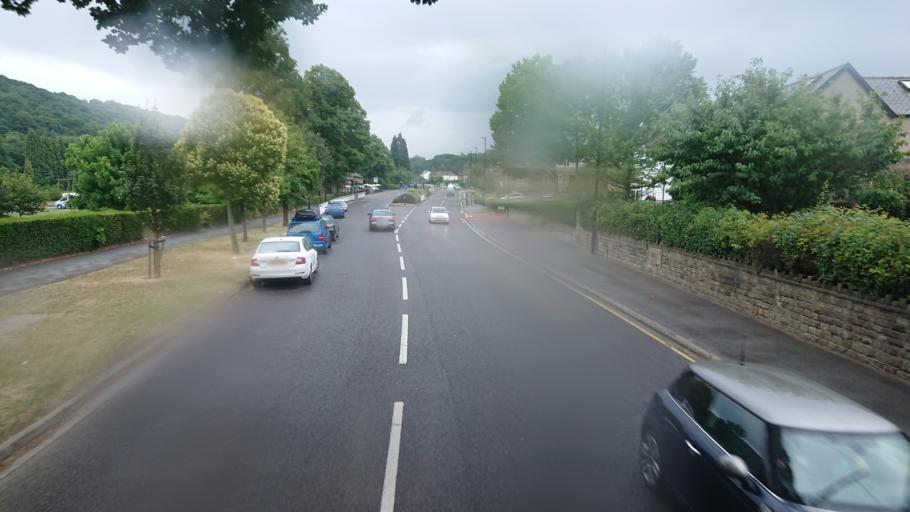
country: GB
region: England
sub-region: Derbyshire
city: Dronfield
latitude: 53.3442
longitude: -1.4997
